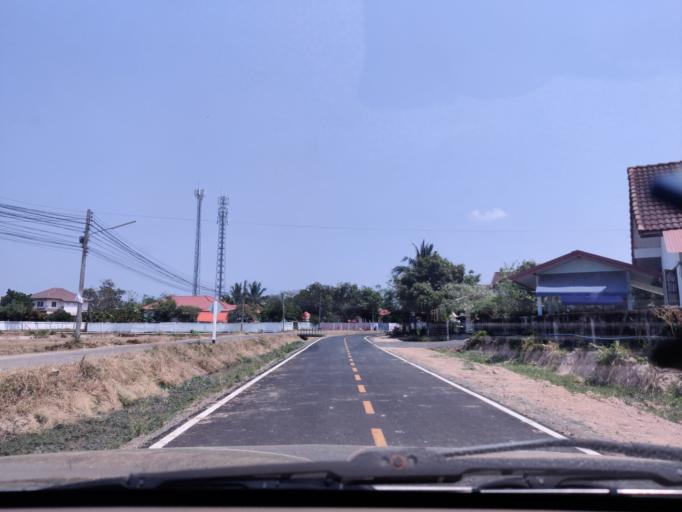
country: TH
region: Sisaket
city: Si Sa Ket
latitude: 15.1079
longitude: 104.3531
